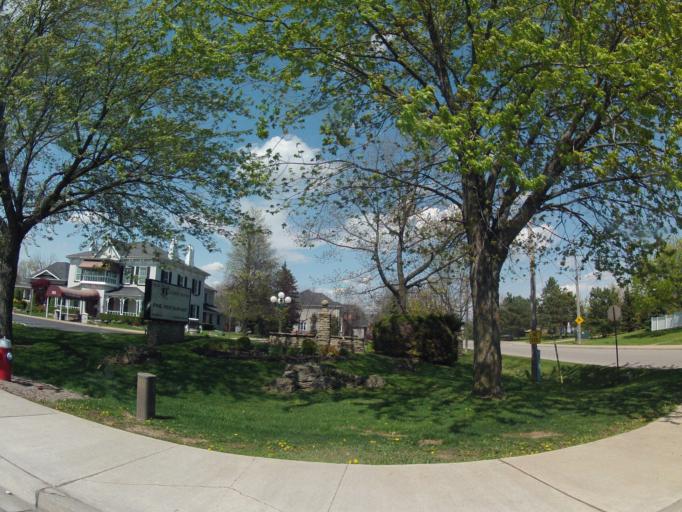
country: CA
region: Ontario
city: Mississauga
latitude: 43.5716
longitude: -79.6999
